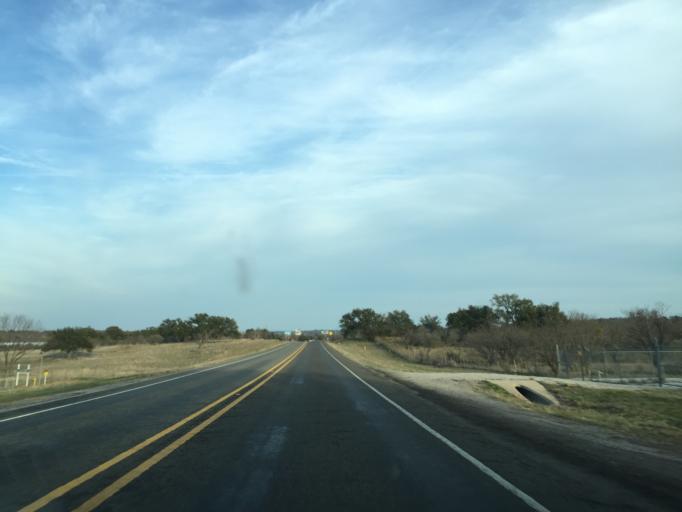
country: US
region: Texas
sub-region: Llano County
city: Llano
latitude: 30.7617
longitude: -98.6408
